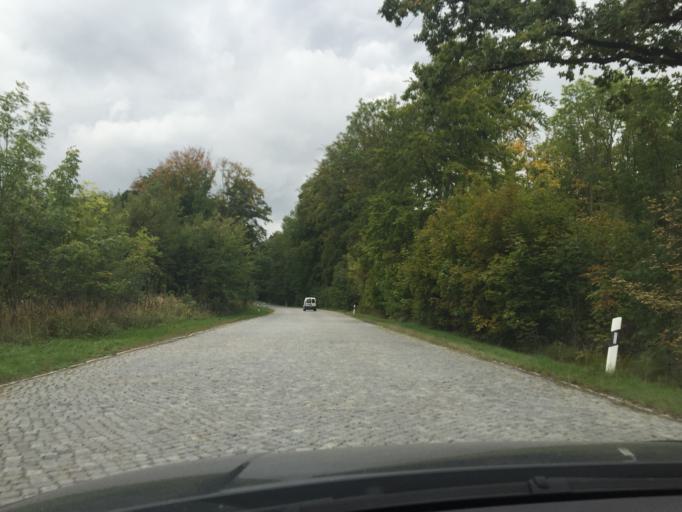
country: DE
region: Thuringia
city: Kleinobringen
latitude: 51.0175
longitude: 11.3026
